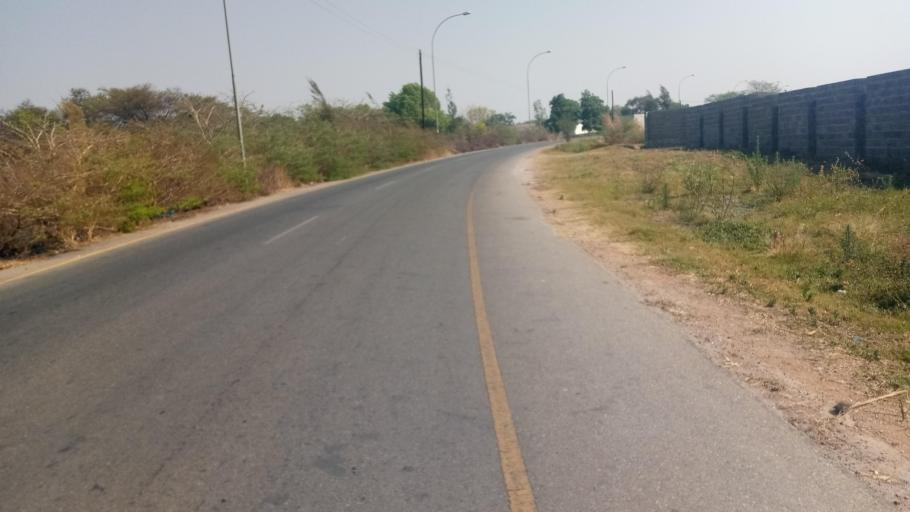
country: ZM
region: Lusaka
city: Lusaka
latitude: -15.4570
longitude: 28.4342
